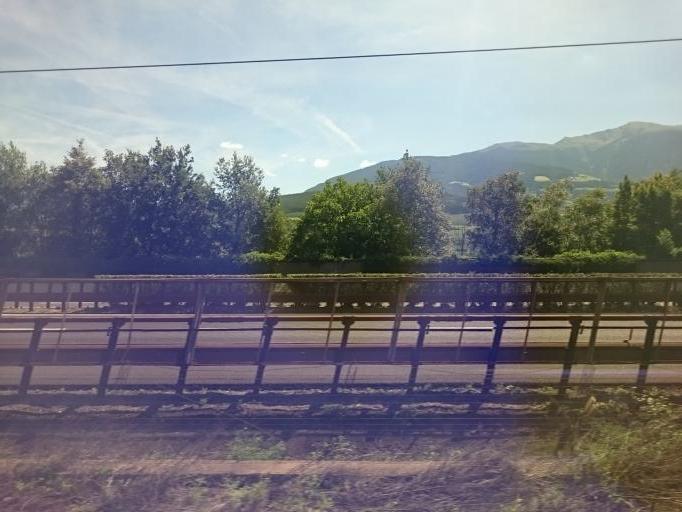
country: IT
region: Trentino-Alto Adige
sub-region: Bolzano
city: Varna
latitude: 46.7400
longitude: 11.6389
